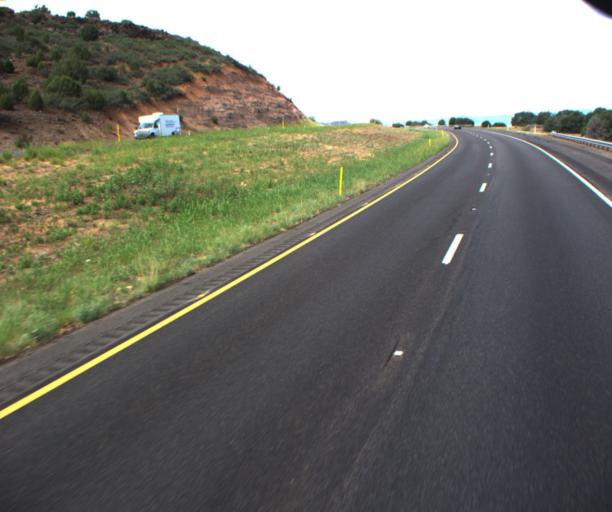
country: US
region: Arizona
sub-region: Yavapai County
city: Camp Verde
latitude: 34.5333
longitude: -111.9767
